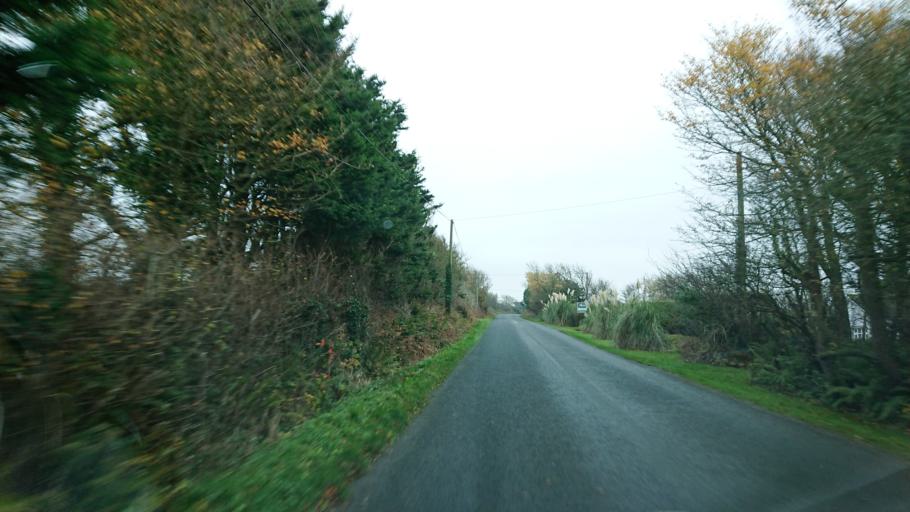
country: IE
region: Munster
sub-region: Waterford
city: Dunmore East
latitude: 52.1683
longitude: -7.0679
